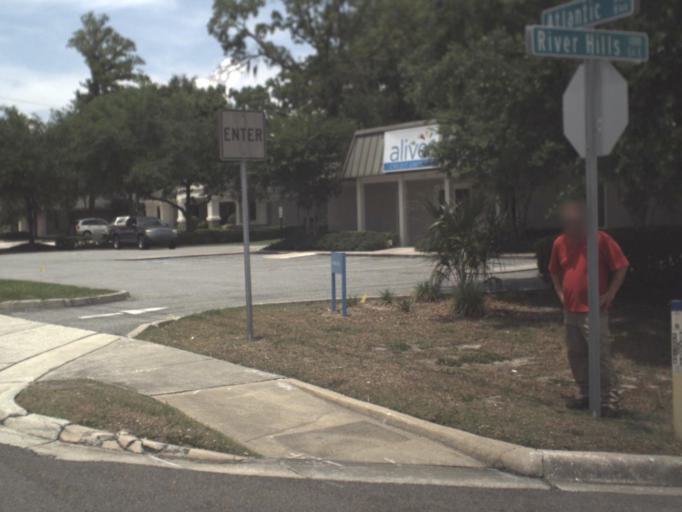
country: US
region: Florida
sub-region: Duval County
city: Jacksonville
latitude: 30.3134
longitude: -81.5968
